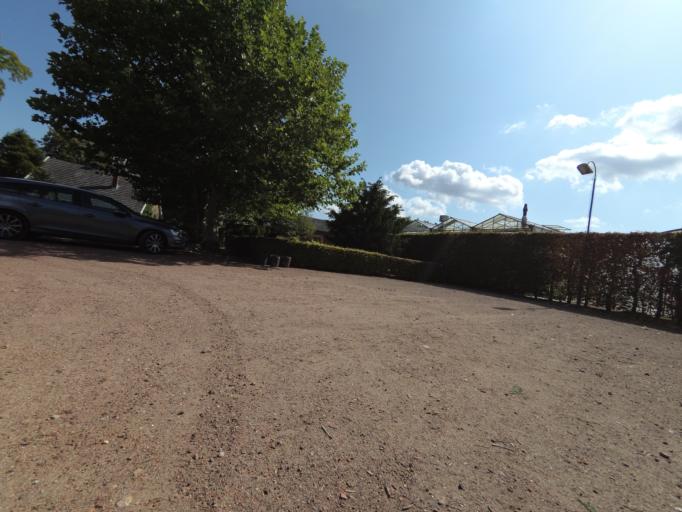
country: NL
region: Overijssel
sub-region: Gemeente Oldenzaal
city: Oldenzaal
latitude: 52.2881
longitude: 6.8619
